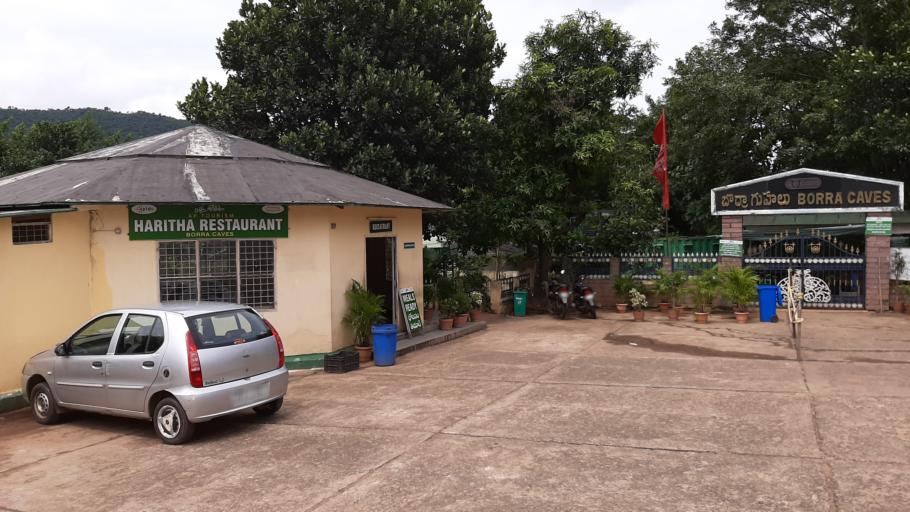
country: IN
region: Andhra Pradesh
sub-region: Vizianagaram District
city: Salur
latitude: 18.2802
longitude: 83.0386
